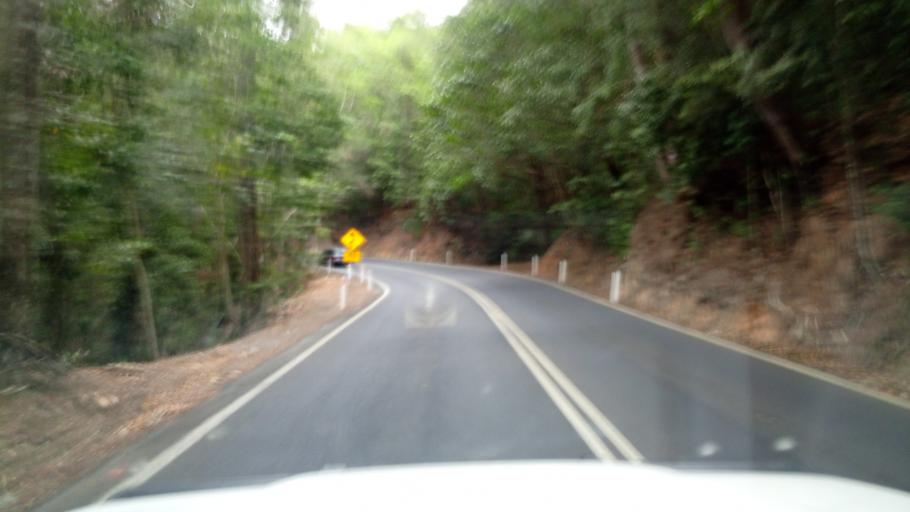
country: AU
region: Queensland
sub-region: Cairns
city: Redlynch
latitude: -16.8445
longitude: 145.6806
